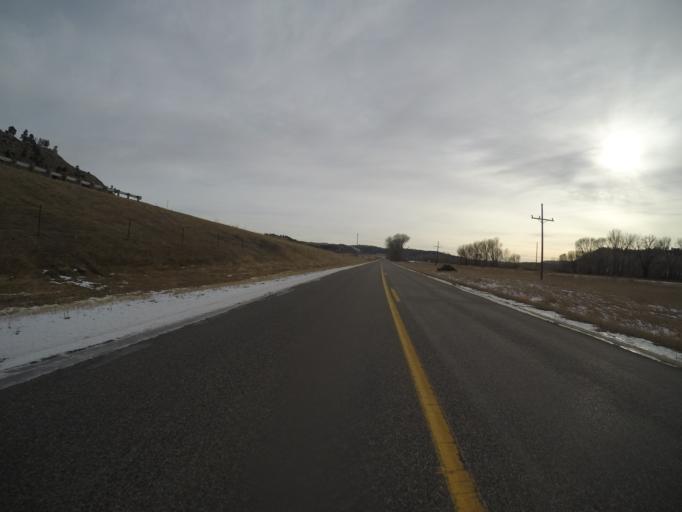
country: US
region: Montana
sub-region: Stillwater County
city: Columbus
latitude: 45.6991
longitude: -109.3856
